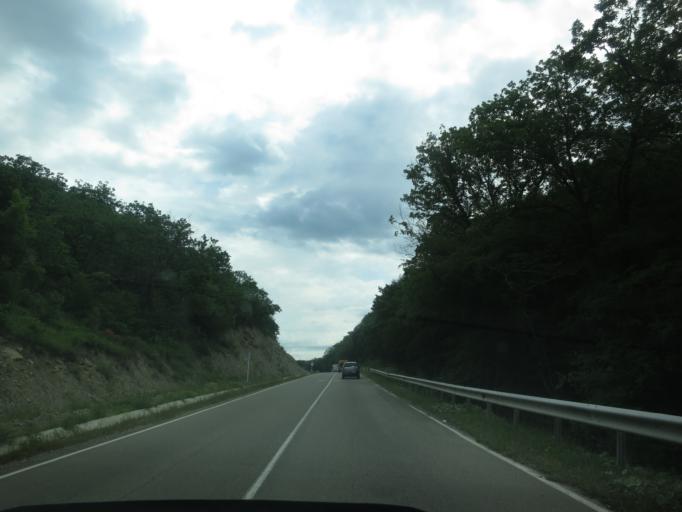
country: GE
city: Didi Lilo
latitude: 41.8097
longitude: 45.1455
